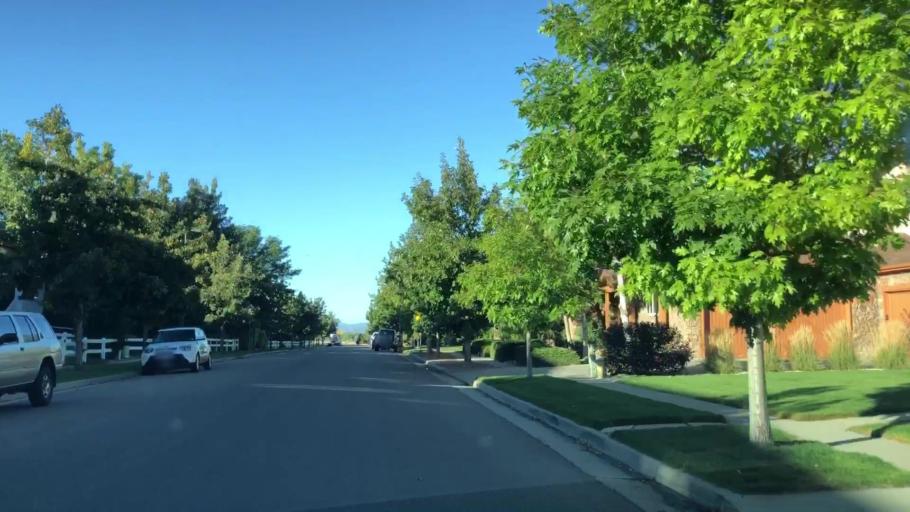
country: US
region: Colorado
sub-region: Larimer County
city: Loveland
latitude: 40.4415
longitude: -105.0265
